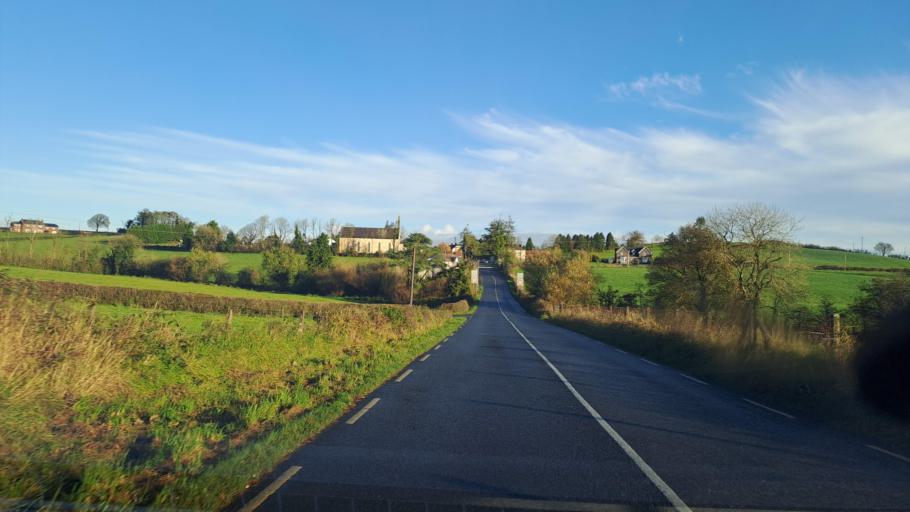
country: IE
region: Ulster
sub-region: County Monaghan
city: Monaghan
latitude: 54.1869
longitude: -6.9908
